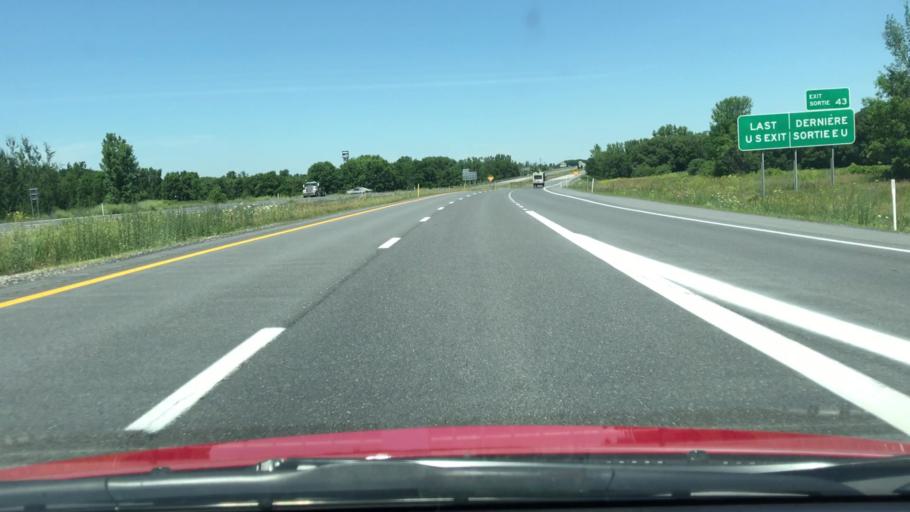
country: US
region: New York
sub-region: Clinton County
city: Champlain
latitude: 44.9834
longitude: -73.4576
